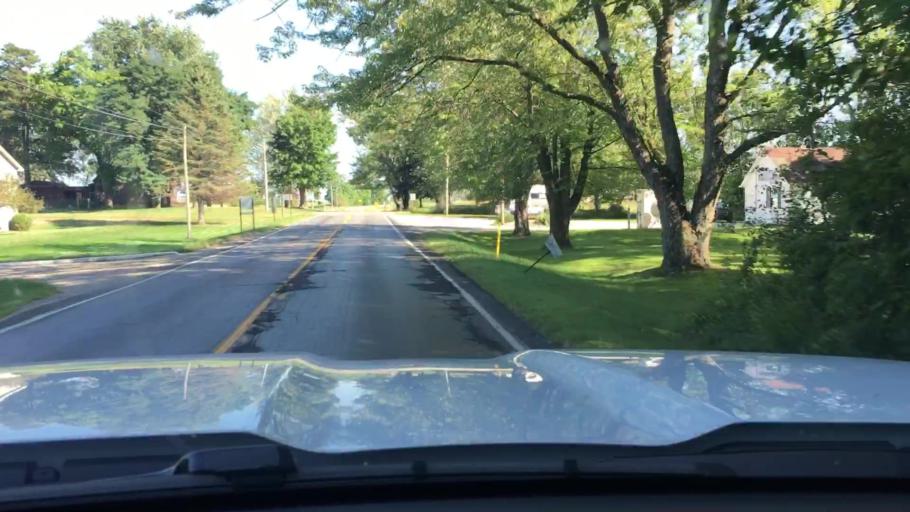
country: US
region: Michigan
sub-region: Muskegon County
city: Ravenna
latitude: 43.1847
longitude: -85.9327
